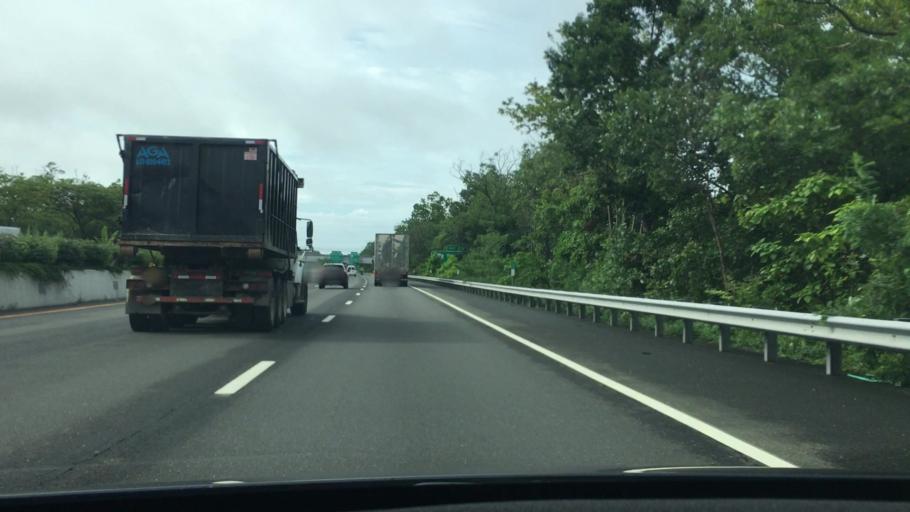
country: US
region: New York
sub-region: Nassau County
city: Seaford
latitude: 40.6781
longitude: -73.4948
